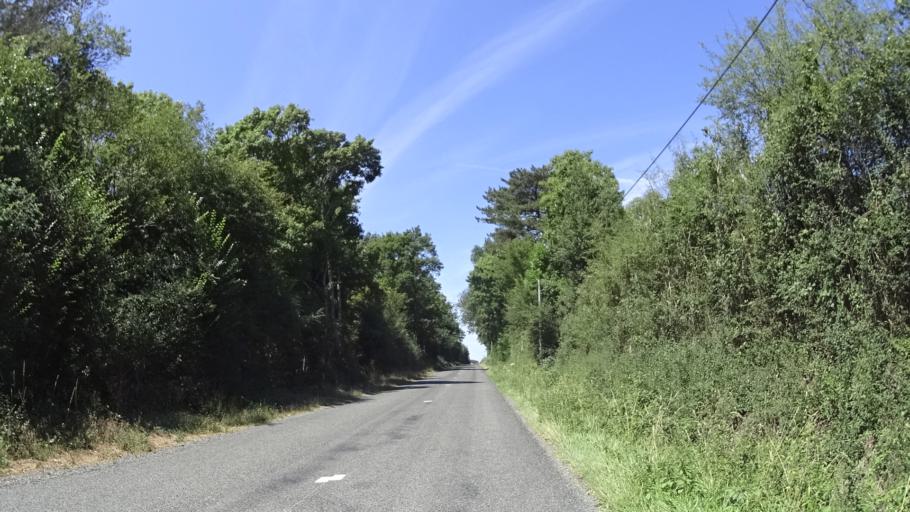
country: FR
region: Pays de la Loire
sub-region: Departement de Maine-et-Loire
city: Grez-Neuville
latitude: 47.6282
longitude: -0.7432
